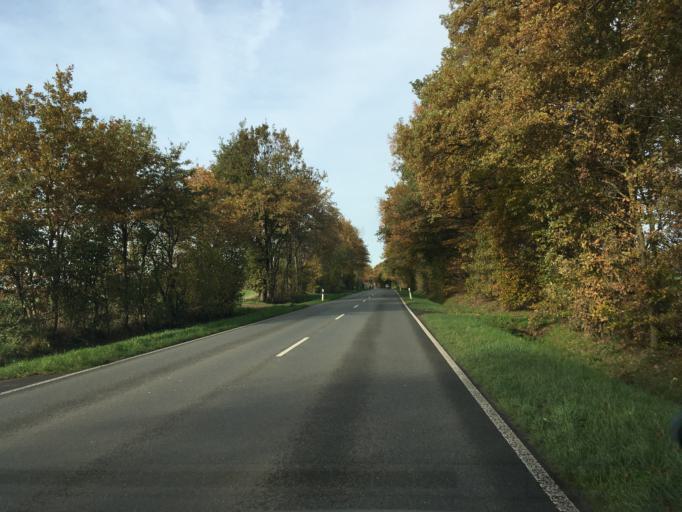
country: DE
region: North Rhine-Westphalia
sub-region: Regierungsbezirk Munster
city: Heiden
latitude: 51.7936
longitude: 6.9590
